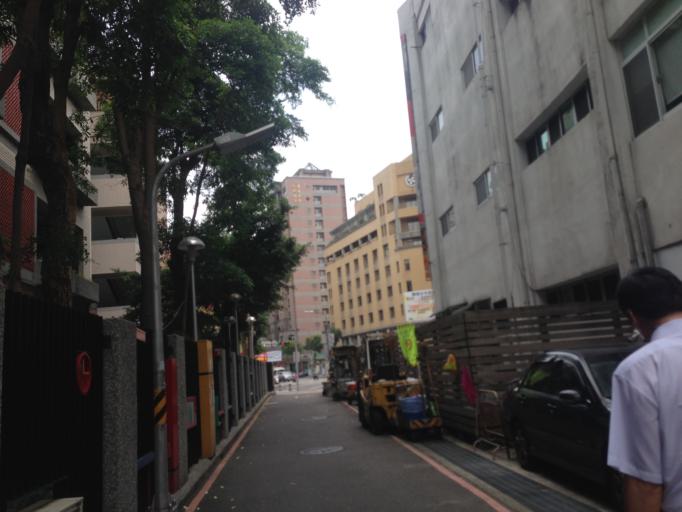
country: TW
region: Taipei
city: Taipei
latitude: 25.0568
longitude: 121.5163
